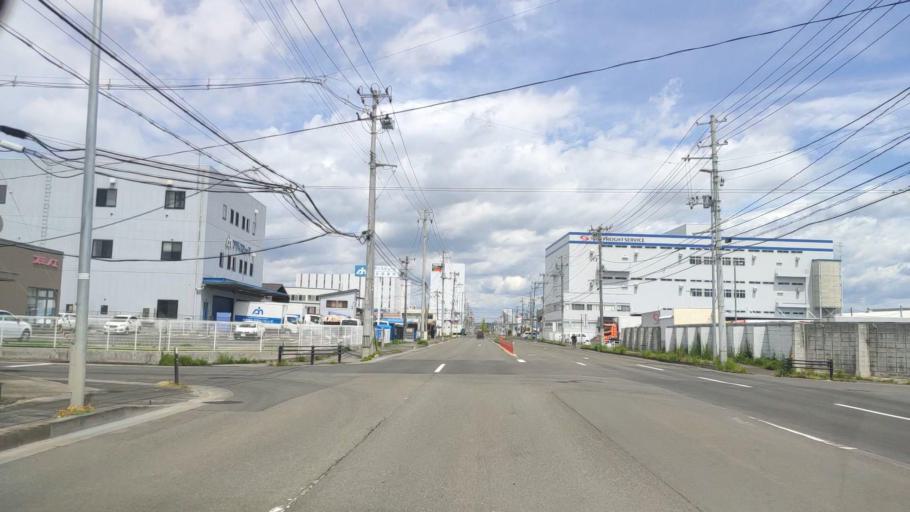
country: JP
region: Miyagi
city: Sendai-shi
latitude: 38.2639
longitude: 140.9432
